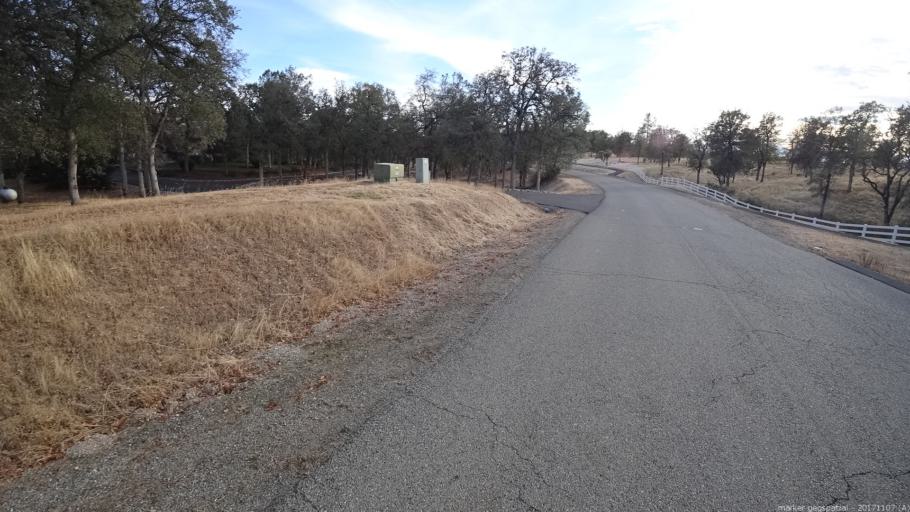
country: US
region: California
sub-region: Shasta County
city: Shasta
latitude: 40.5104
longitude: -122.4740
